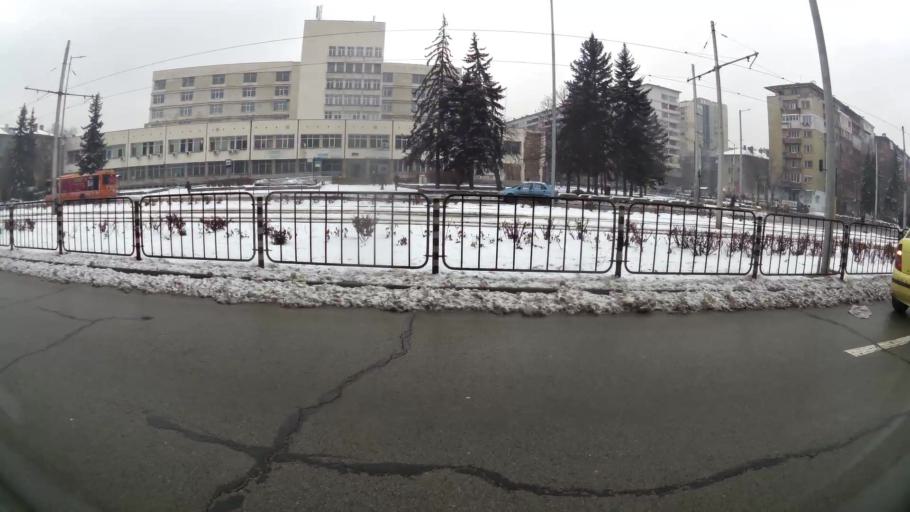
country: BG
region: Sofia-Capital
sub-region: Stolichna Obshtina
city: Sofia
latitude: 42.7130
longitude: 23.3160
